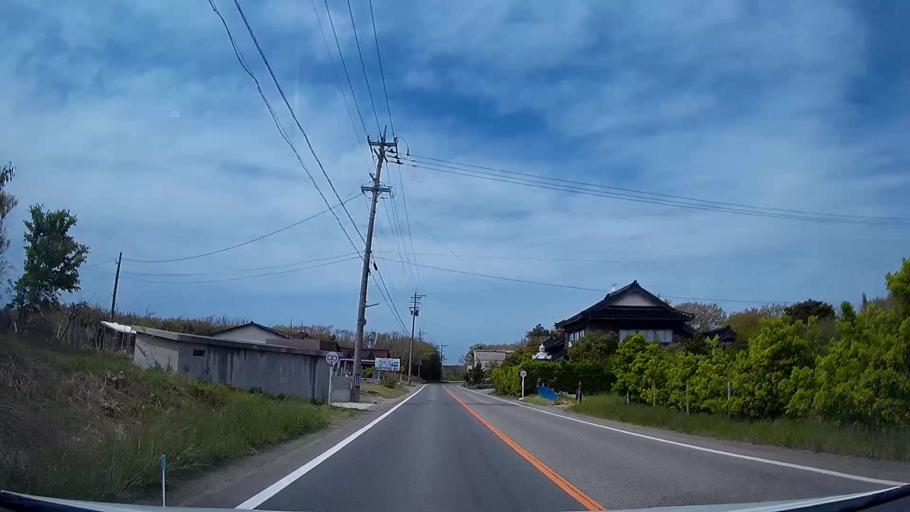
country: JP
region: Ishikawa
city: Hakui
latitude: 36.9677
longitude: 136.7725
